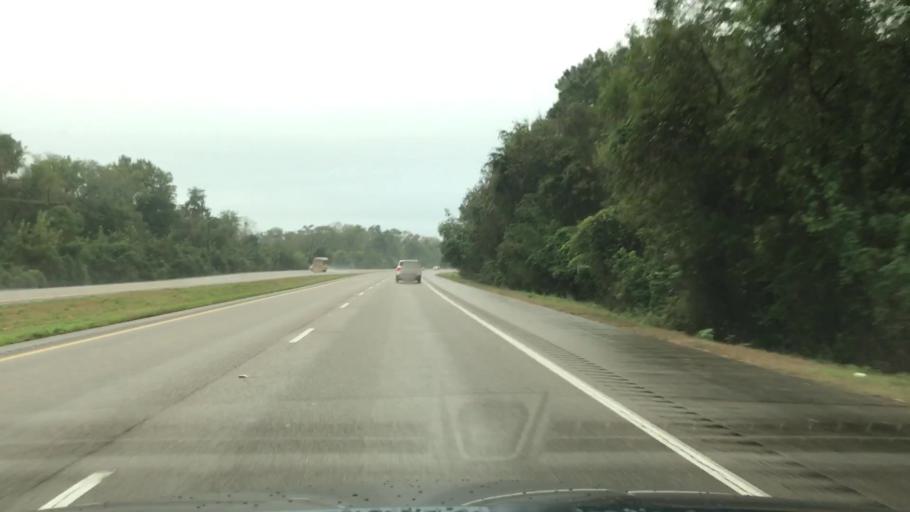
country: US
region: Louisiana
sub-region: Saint Charles Parish
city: Des Allemands
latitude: 29.8464
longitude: -90.4480
